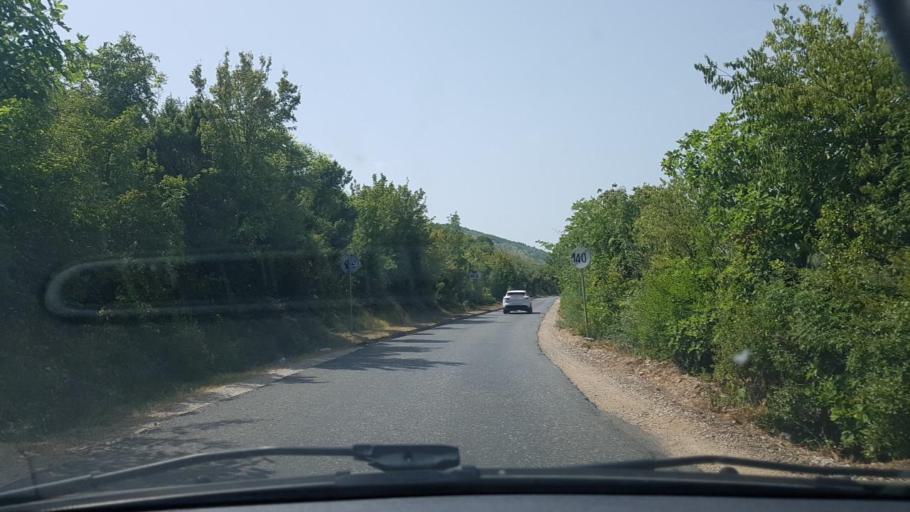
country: HR
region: Dubrovacko-Neretvanska
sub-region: Grad Dubrovnik
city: Metkovic
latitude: 43.0359
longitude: 17.7236
